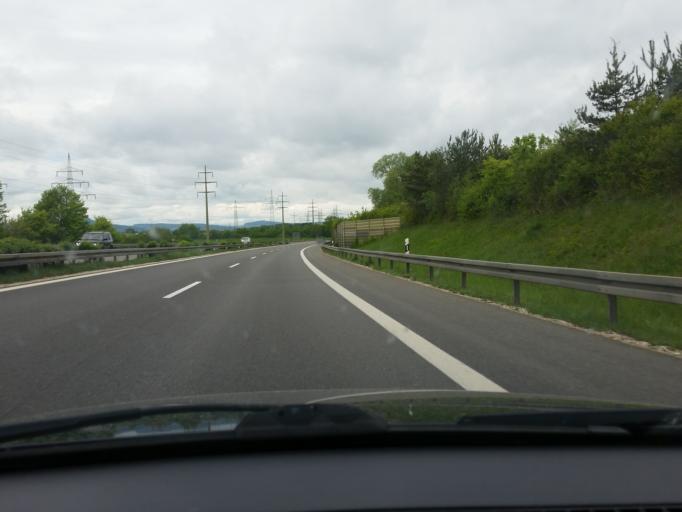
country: DE
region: Baden-Wuerttemberg
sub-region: Freiburg Region
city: Volkertshausen
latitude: 47.7969
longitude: 8.8683
